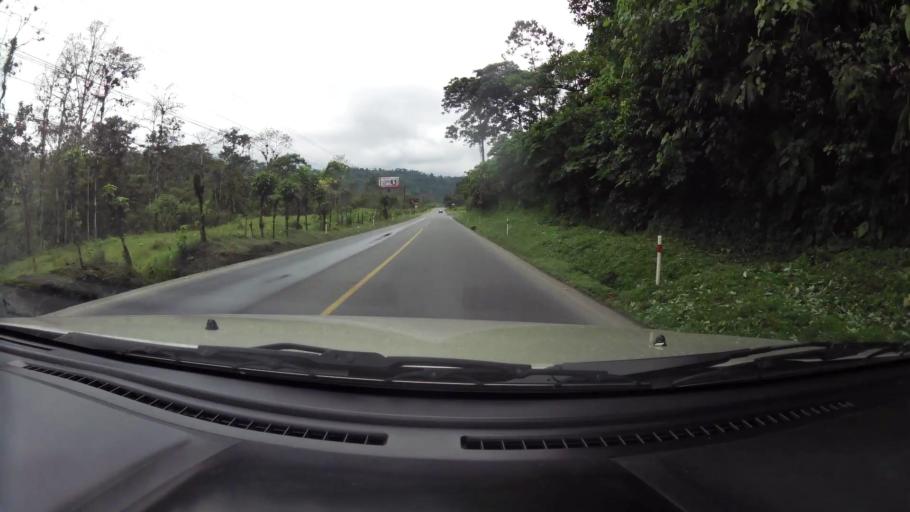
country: EC
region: Santo Domingo de los Tsachilas
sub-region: Canton Santo Domingo de los Colorados
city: Santo Domingo de los Colorados
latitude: -0.2676
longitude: -79.0875
